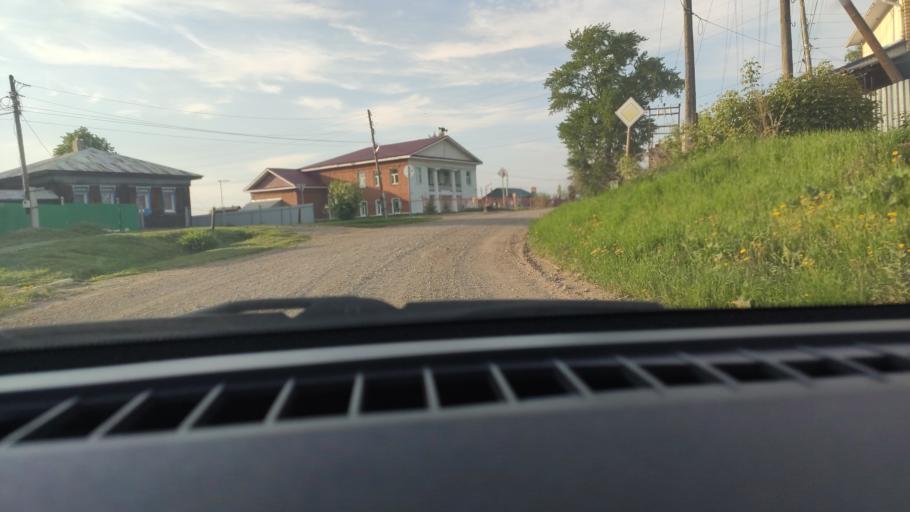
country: RU
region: Perm
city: Kultayevo
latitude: 57.9309
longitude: 56.0166
